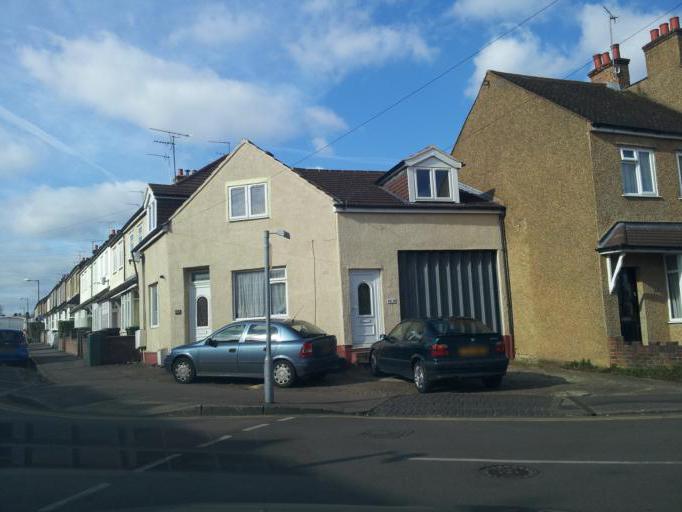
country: GB
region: England
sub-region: Hertfordshire
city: St Albans
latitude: 51.7490
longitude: -0.3112
